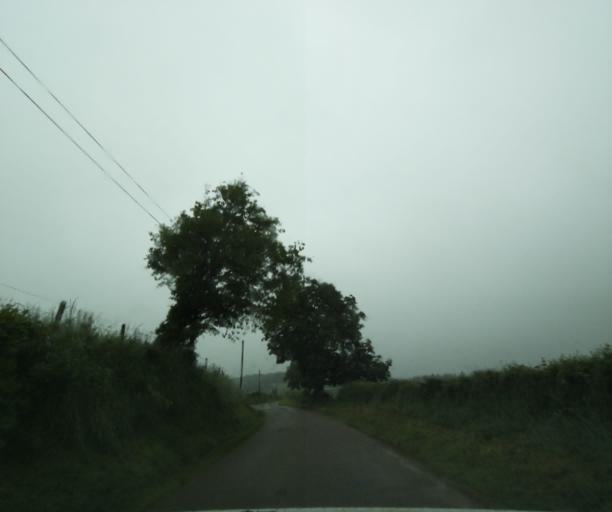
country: FR
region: Bourgogne
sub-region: Departement de Saone-et-Loire
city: Charolles
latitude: 46.4148
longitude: 4.3825
